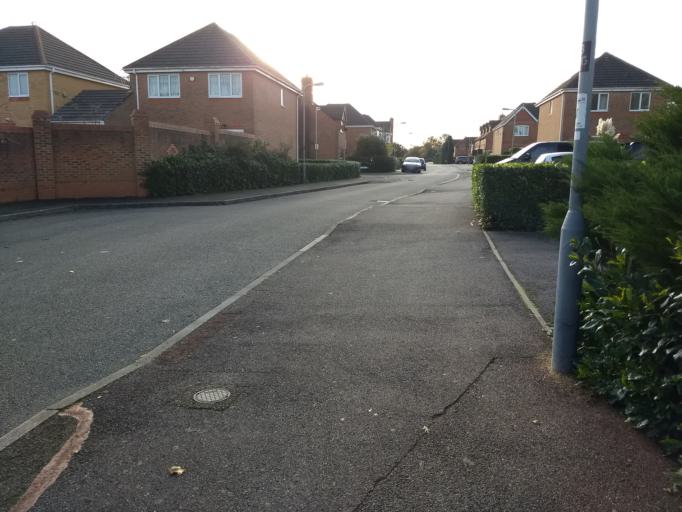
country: GB
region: England
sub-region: Buckinghamshire
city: Bletchley
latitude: 52.0034
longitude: -0.7585
